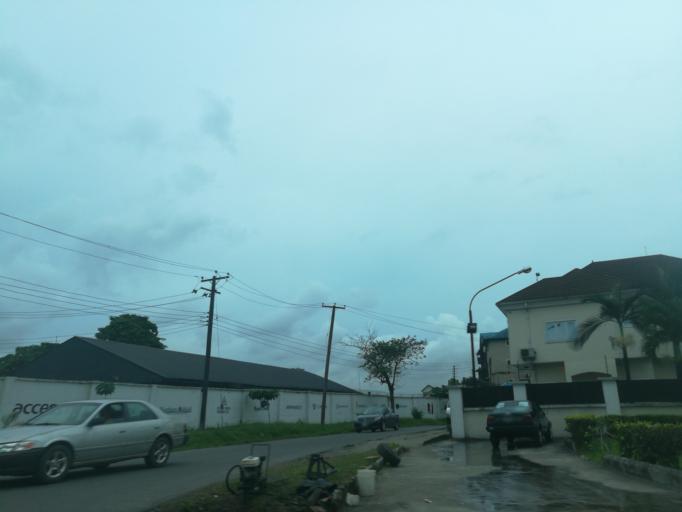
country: NG
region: Rivers
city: Port Harcourt
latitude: 4.8209
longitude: 7.0009
